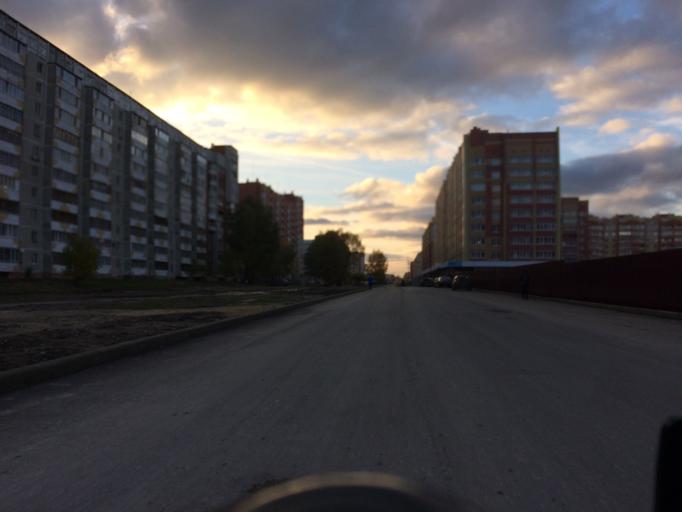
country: RU
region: Mariy-El
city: Yoshkar-Ola
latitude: 56.6379
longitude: 47.9333
